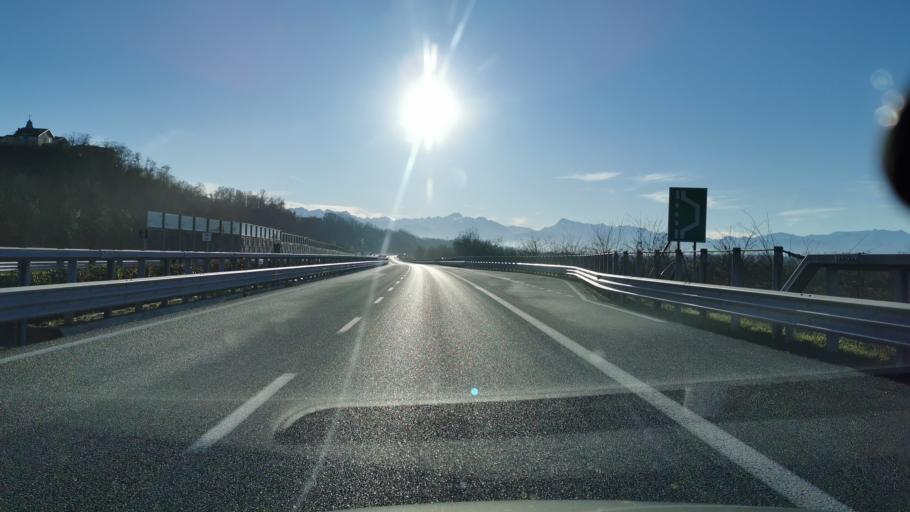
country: IT
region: Piedmont
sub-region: Provincia di Cuneo
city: Montanera
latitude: 44.4674
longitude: 7.6669
